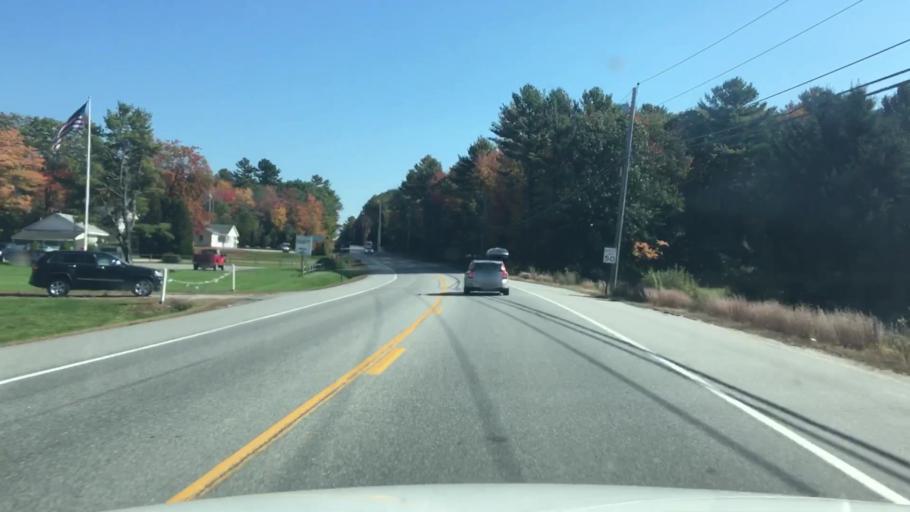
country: US
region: Maine
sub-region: Sagadahoc County
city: Topsham
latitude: 43.9622
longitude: -70.0141
